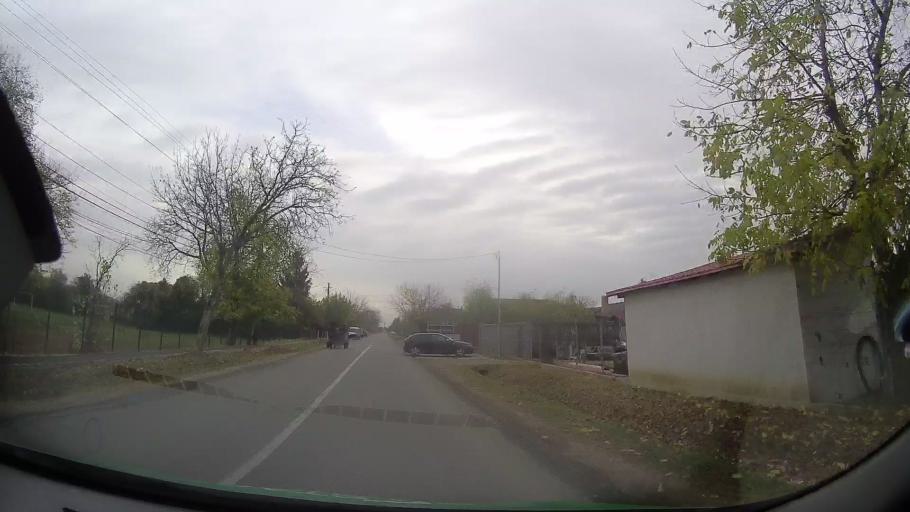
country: RO
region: Prahova
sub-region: Comuna Valea Calugareasca
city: Pantazi
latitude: 44.9160
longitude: 26.1569
